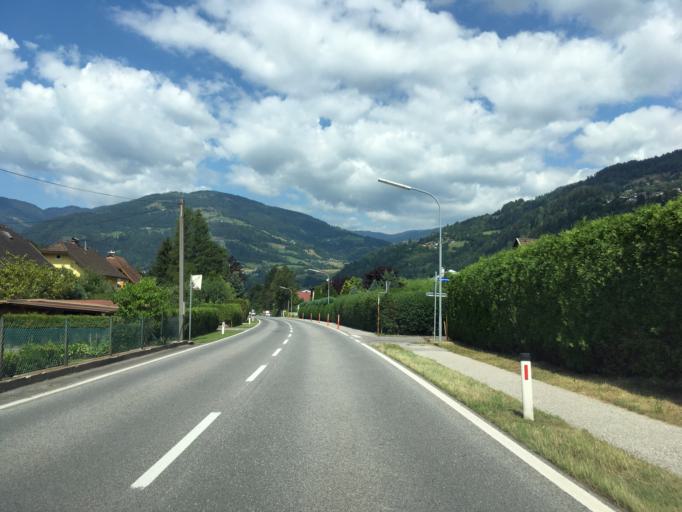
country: AT
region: Carinthia
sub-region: Politischer Bezirk Spittal an der Drau
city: Radenthein
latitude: 46.7899
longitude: 13.7291
